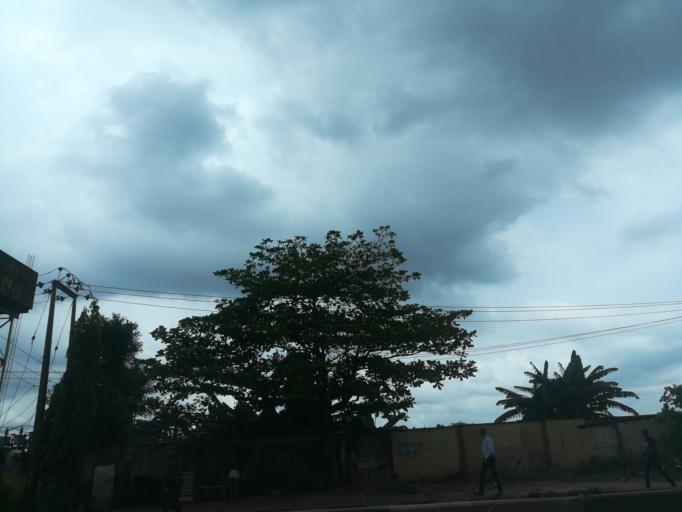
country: NG
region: Lagos
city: Oshodi
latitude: 6.5511
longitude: 3.3537
